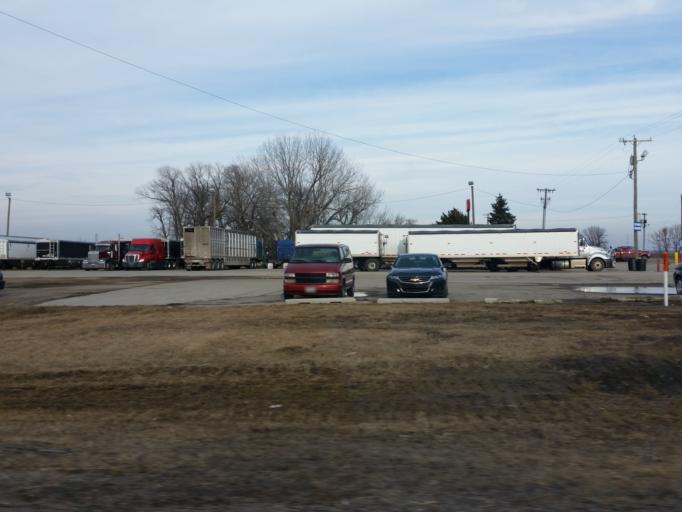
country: US
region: North Dakota
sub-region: Cass County
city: Casselton
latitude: 46.8764
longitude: -97.2107
